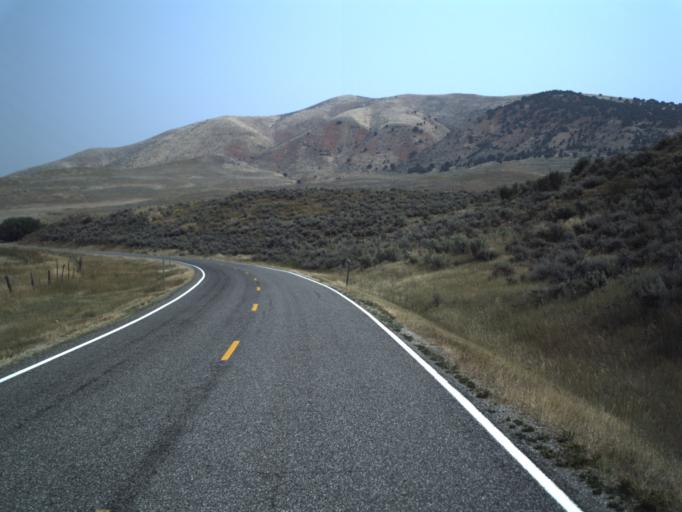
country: US
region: Utah
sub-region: Summit County
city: Coalville
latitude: 40.9871
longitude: -111.5289
